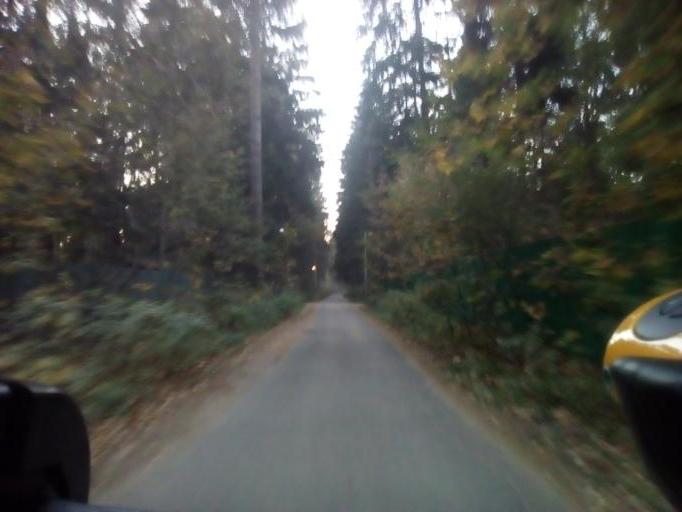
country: RU
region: Moskovskaya
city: Kratovo
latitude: 55.6083
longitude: 38.1650
